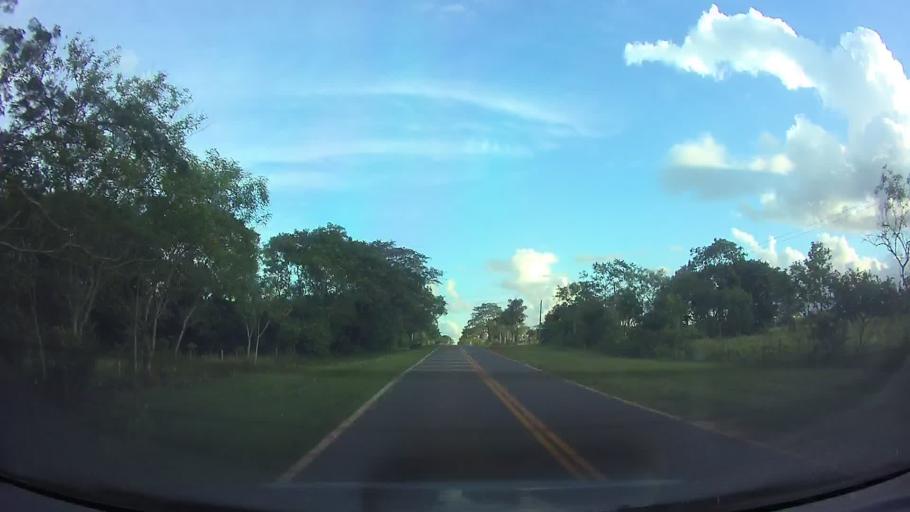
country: PY
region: Paraguari
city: Ybycui
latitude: -25.9764
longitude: -57.0737
